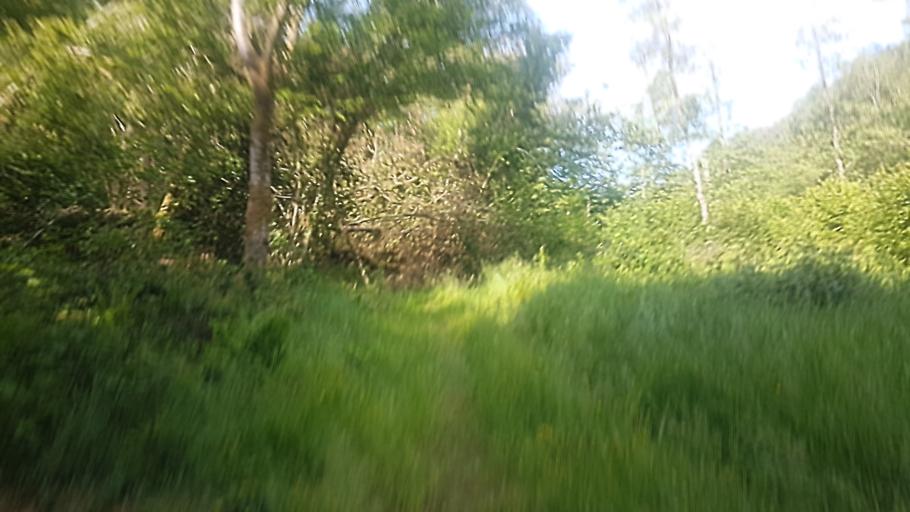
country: BE
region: Wallonia
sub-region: Province de Namur
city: Couvin
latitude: 50.0466
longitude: 4.5876
